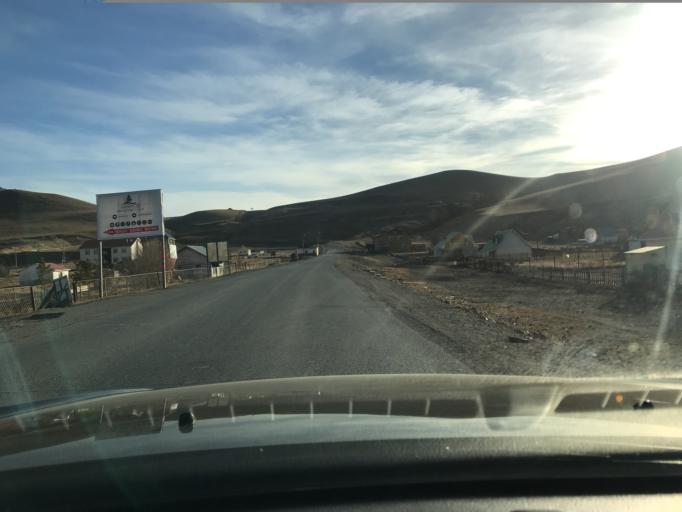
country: MN
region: Central Aimak
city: Dzuunmod
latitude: 47.8183
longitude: 107.3302
